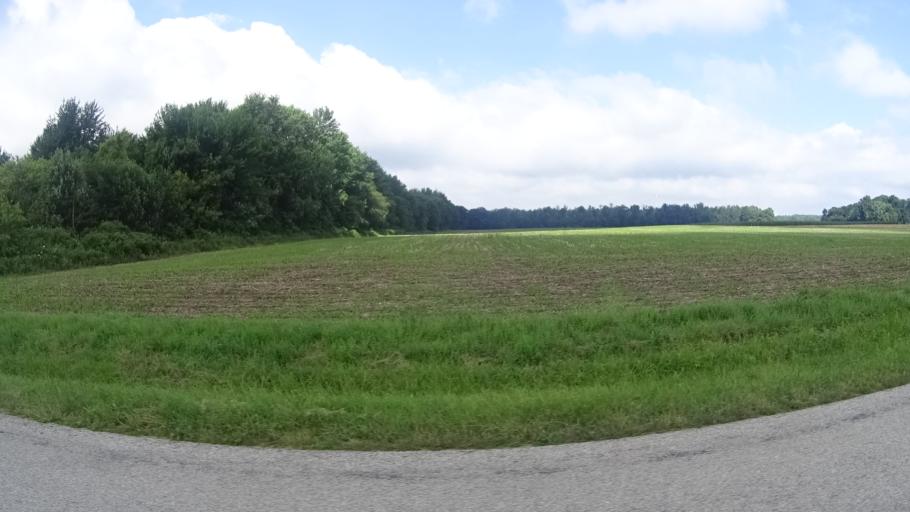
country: US
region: Ohio
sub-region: Huron County
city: Wakeman
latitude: 41.2961
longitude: -82.4657
